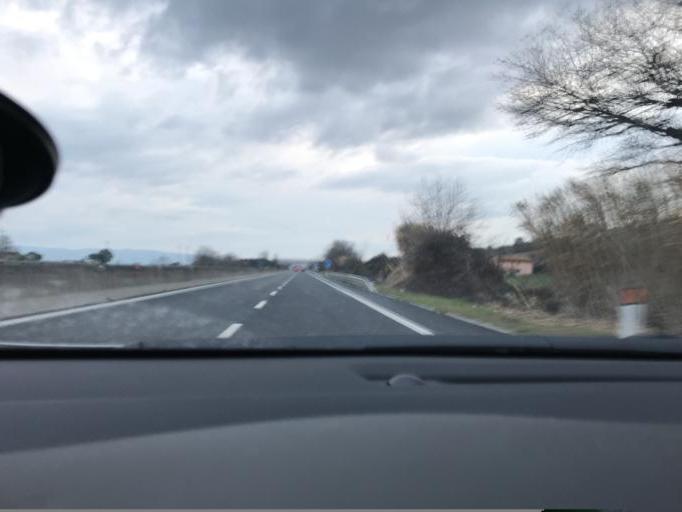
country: IT
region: Umbria
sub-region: Provincia di Perugia
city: Petrignano
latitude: 43.1314
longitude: 12.5219
